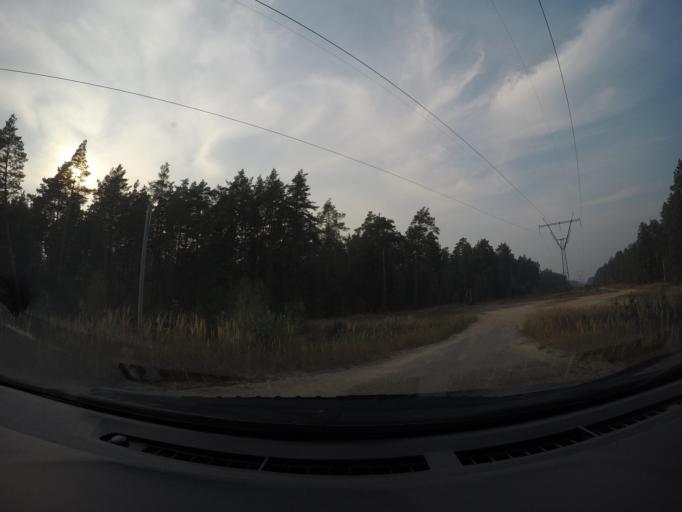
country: RU
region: Moskovskaya
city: Imeni Tsyurupy
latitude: 55.4967
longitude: 38.6883
